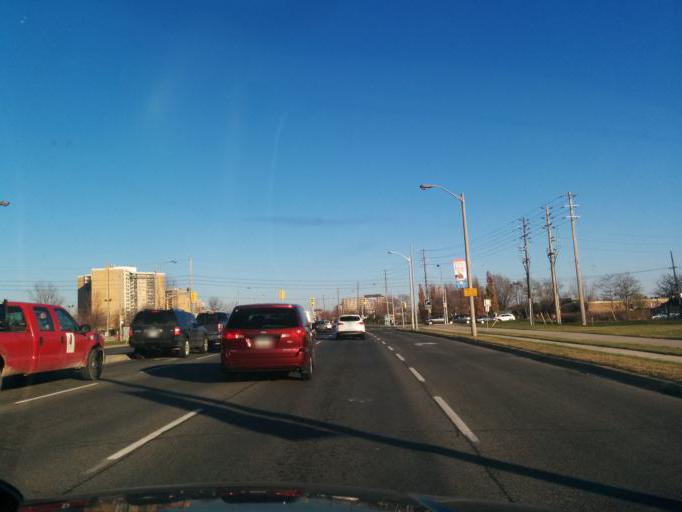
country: CA
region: Ontario
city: Etobicoke
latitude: 43.6742
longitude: -79.5644
